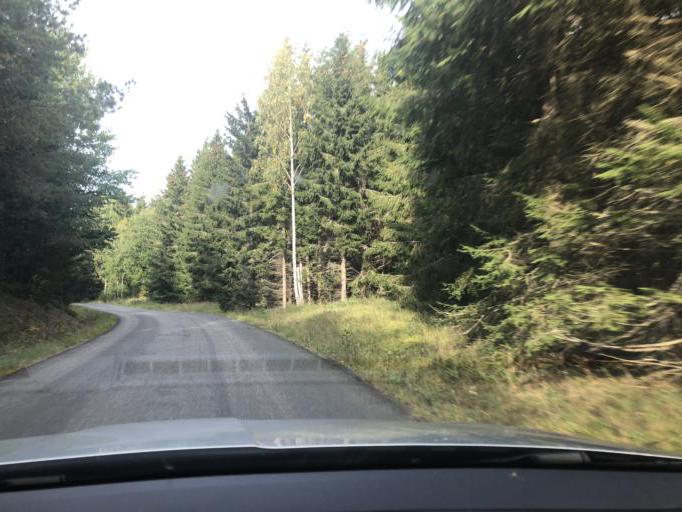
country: SE
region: Joenkoeping
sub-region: Vetlanda Kommun
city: Ekenassjon
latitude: 57.4966
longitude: 14.9044
